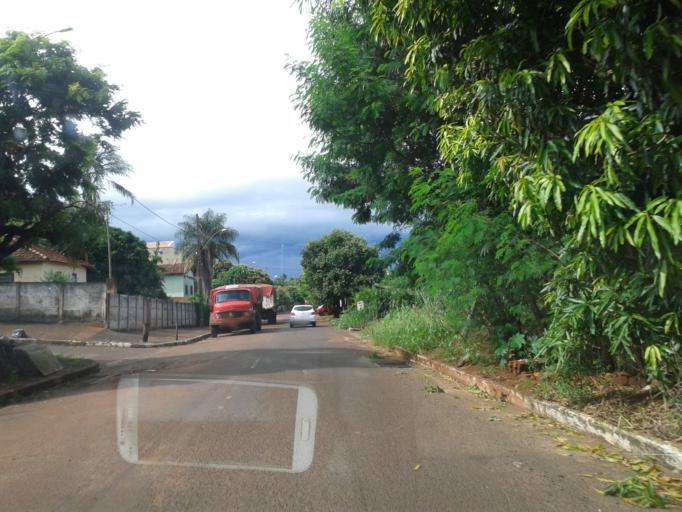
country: BR
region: Minas Gerais
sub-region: Ituiutaba
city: Ituiutaba
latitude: -18.9829
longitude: -49.4746
